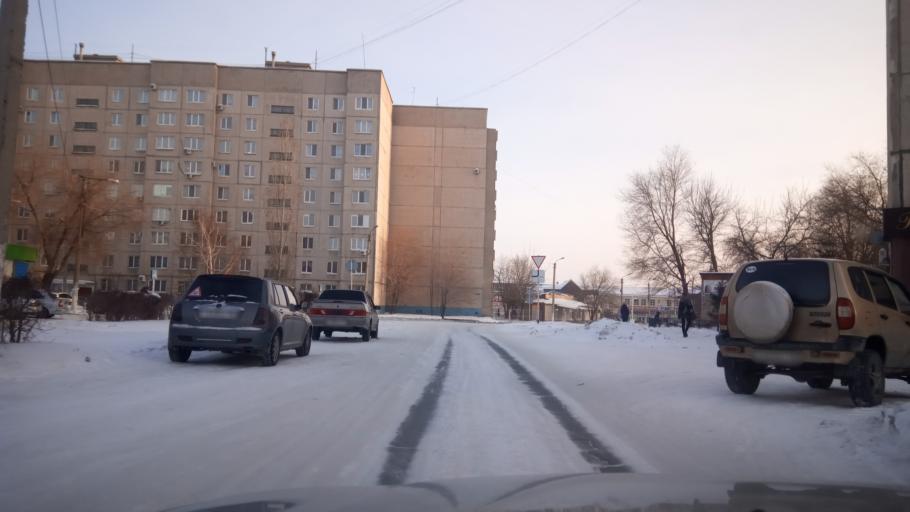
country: RU
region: Orenburg
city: Novotroitsk
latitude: 51.1934
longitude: 58.2903
